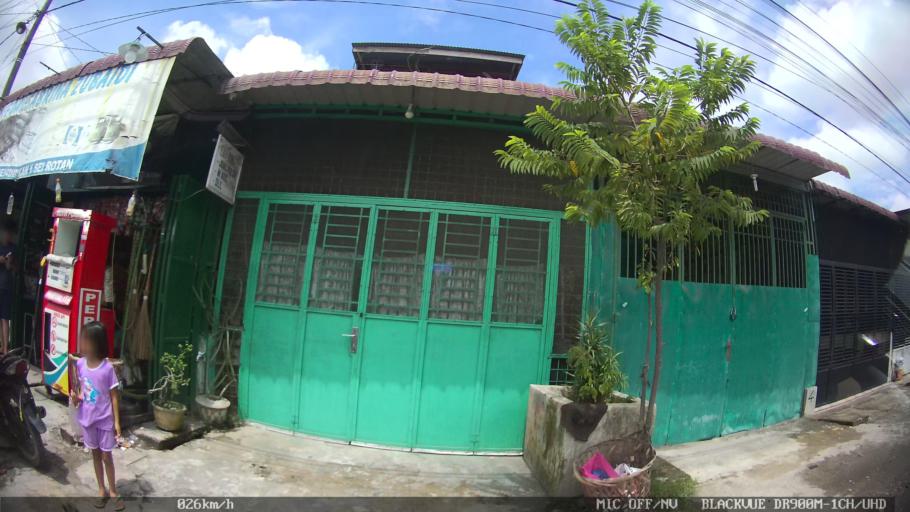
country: ID
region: North Sumatra
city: Percut
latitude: 3.6089
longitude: 98.7815
